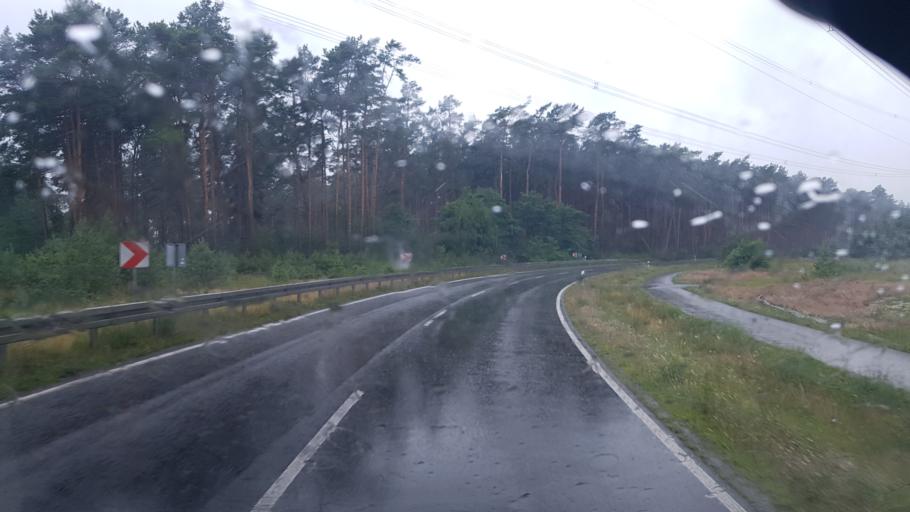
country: DE
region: Brandenburg
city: Golssen
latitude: 52.0487
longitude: 13.6078
